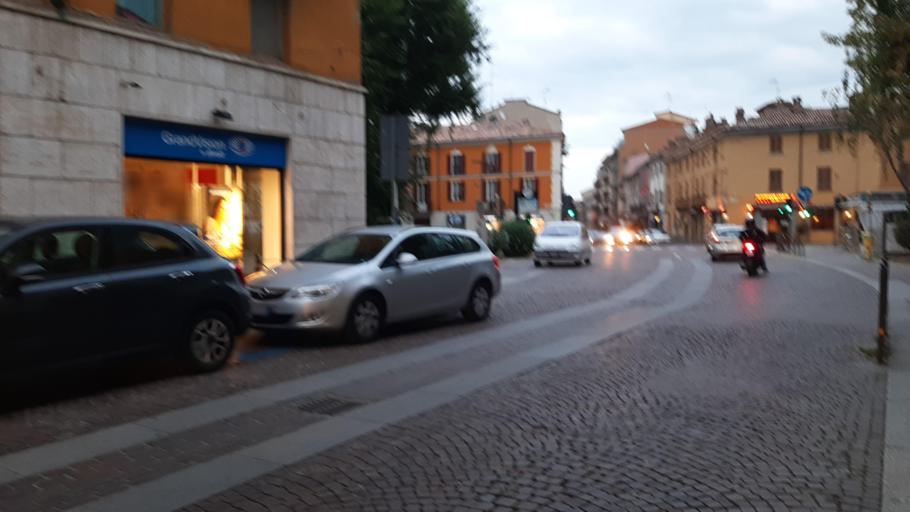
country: IT
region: Lombardy
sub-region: Provincia di Pavia
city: Voghera
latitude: 44.9944
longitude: 9.0118
